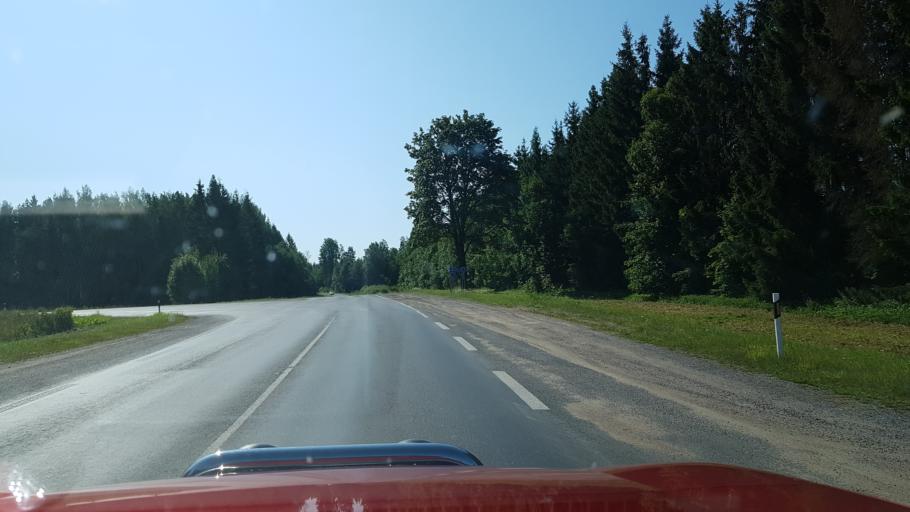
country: EE
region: Polvamaa
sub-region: Polva linn
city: Polva
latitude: 58.0004
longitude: 26.9297
